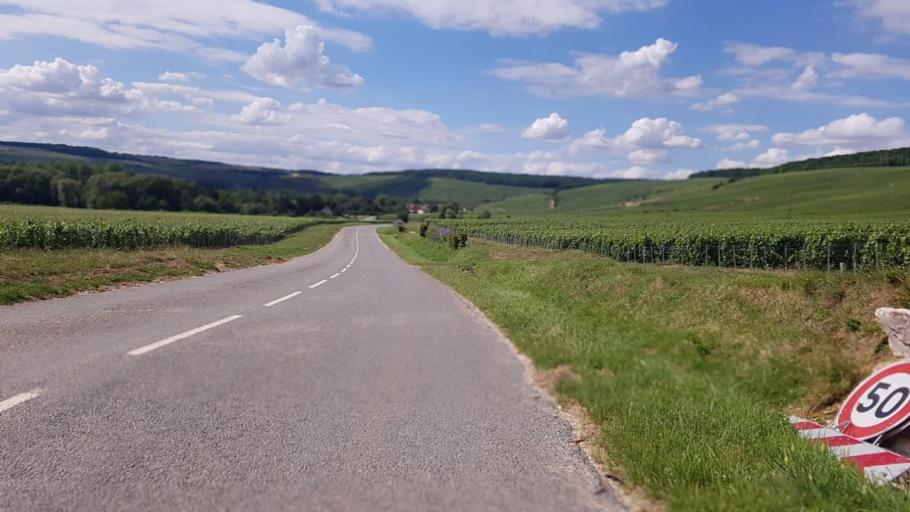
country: FR
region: Picardie
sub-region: Departement de l'Aisne
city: Crezancy
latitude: 49.0668
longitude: 3.5678
